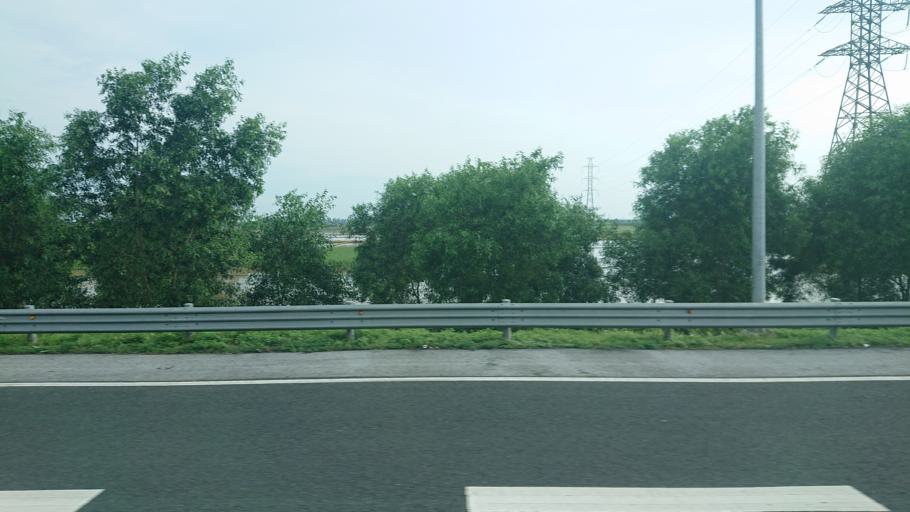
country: VN
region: Hai Phong
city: An Lao
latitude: 20.7914
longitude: 106.5518
